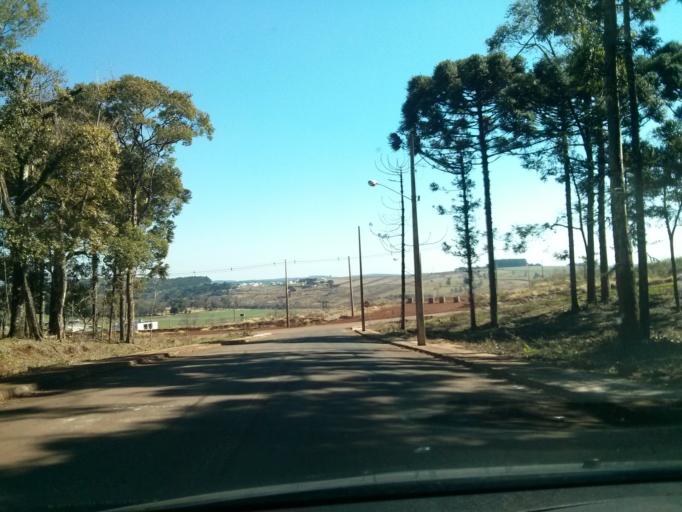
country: BR
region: Santa Catarina
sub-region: Chapeco
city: Chapeco
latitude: -27.0888
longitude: -52.6919
